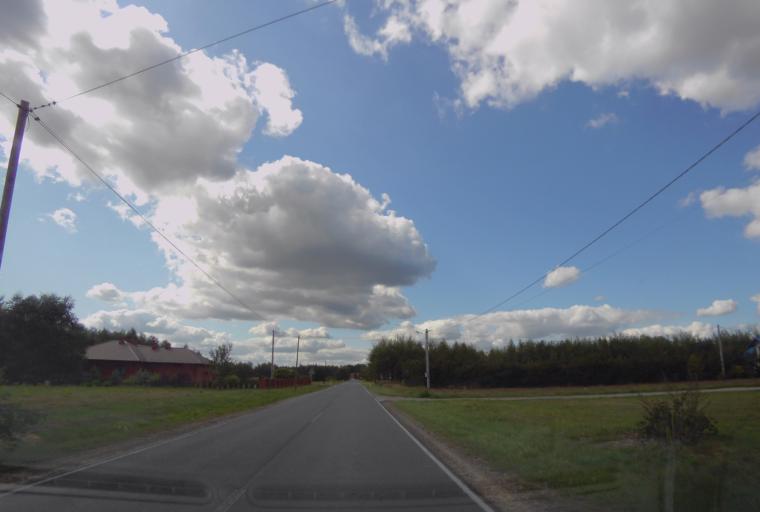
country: PL
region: Subcarpathian Voivodeship
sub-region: Powiat kolbuszowski
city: Majdan Krolewski
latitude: 50.3950
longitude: 21.7733
